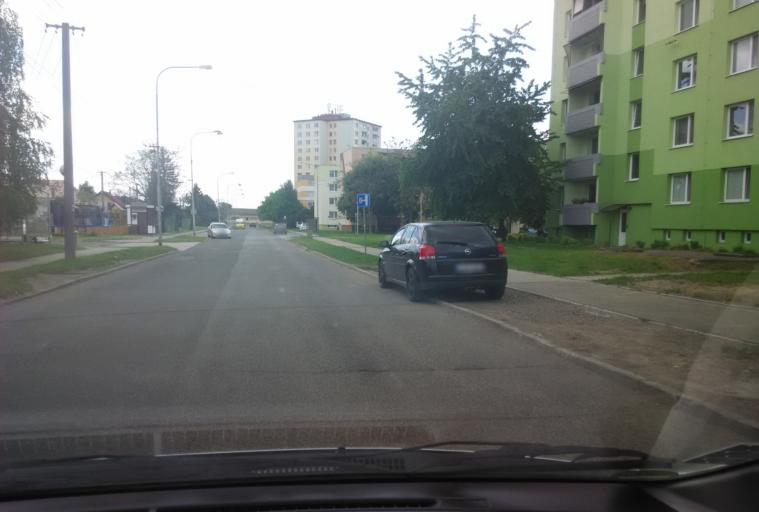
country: SK
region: Nitriansky
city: Levice
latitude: 48.2066
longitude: 18.6118
